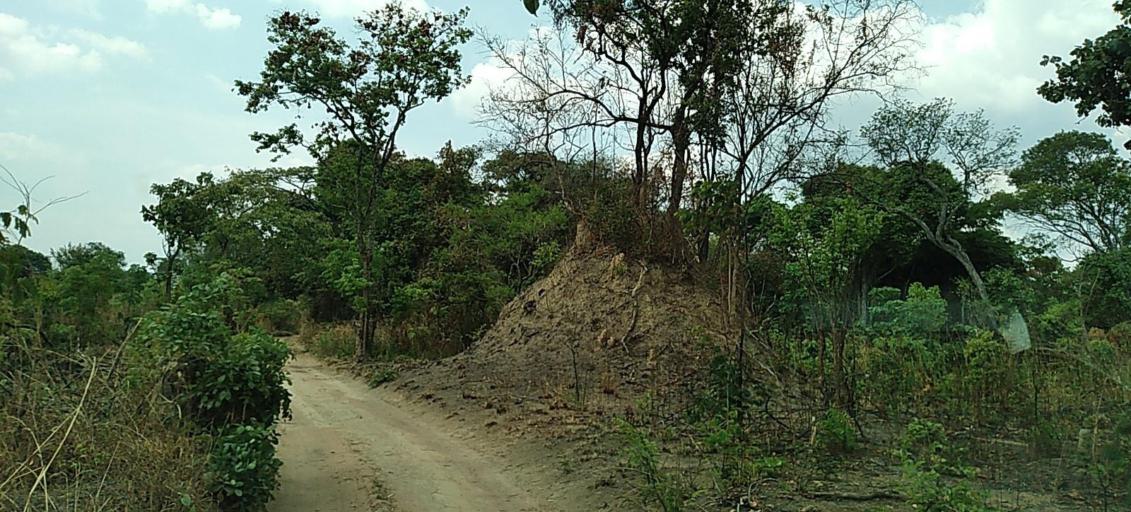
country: ZM
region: Copperbelt
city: Chililabombwe
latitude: -12.3301
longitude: 27.7481
